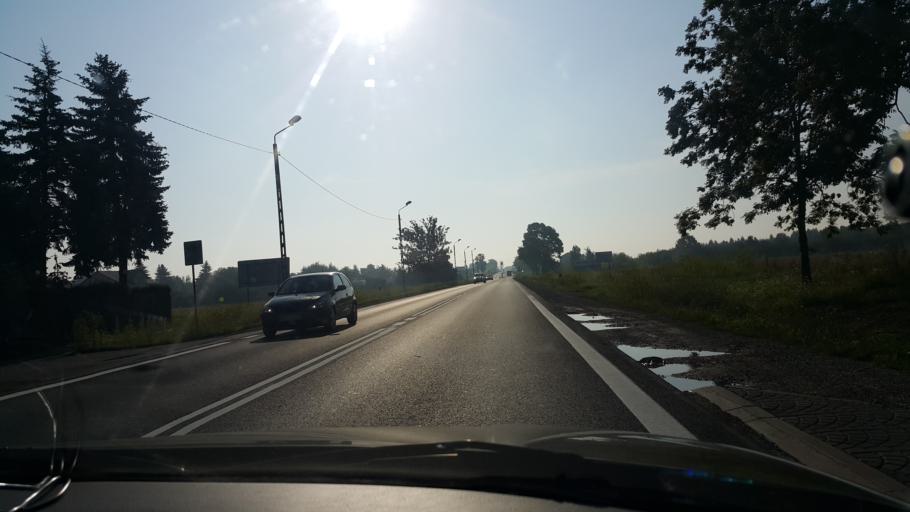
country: PL
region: Masovian Voivodeship
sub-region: Radom
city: Radom
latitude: 51.4144
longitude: 21.2161
